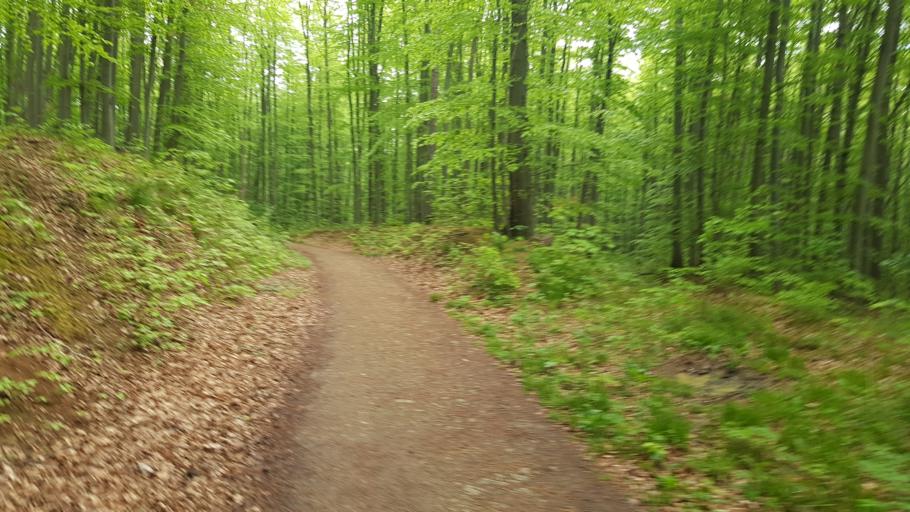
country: DE
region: Saxony-Anhalt
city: Neinstedt
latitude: 51.7396
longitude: 11.0680
